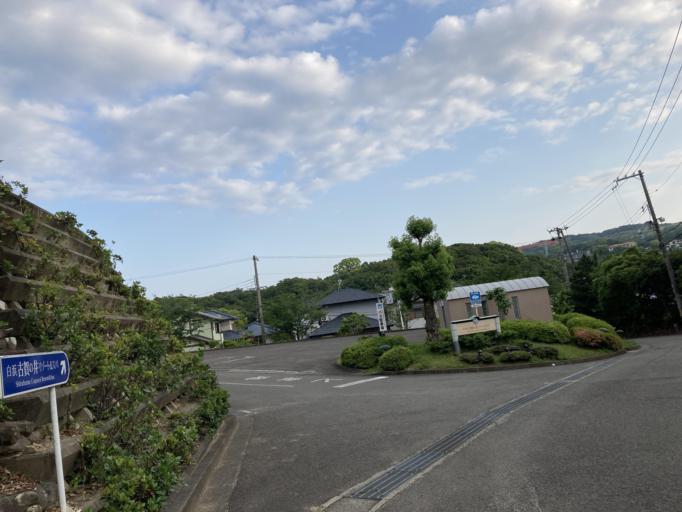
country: JP
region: Wakayama
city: Tanabe
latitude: 33.6828
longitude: 135.3572
